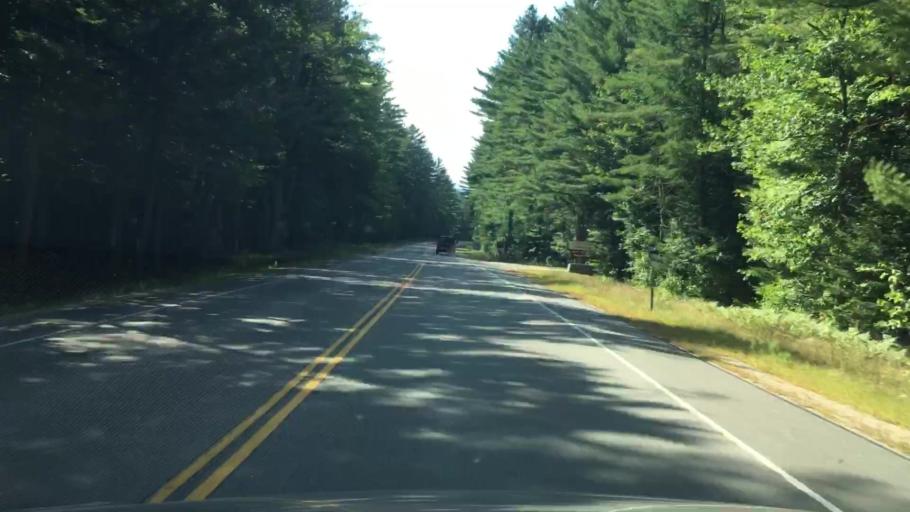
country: US
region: New Hampshire
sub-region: Carroll County
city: Tamworth
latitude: 43.9947
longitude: -71.3347
